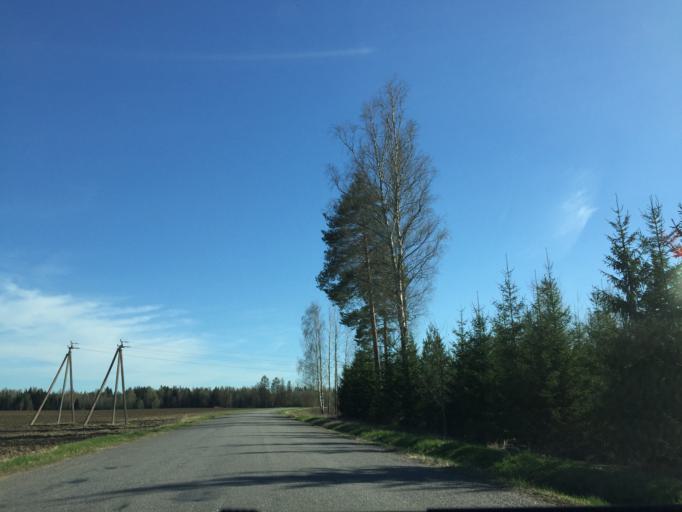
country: EE
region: Valgamaa
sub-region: Valga linn
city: Valga
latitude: 57.8562
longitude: 26.2534
